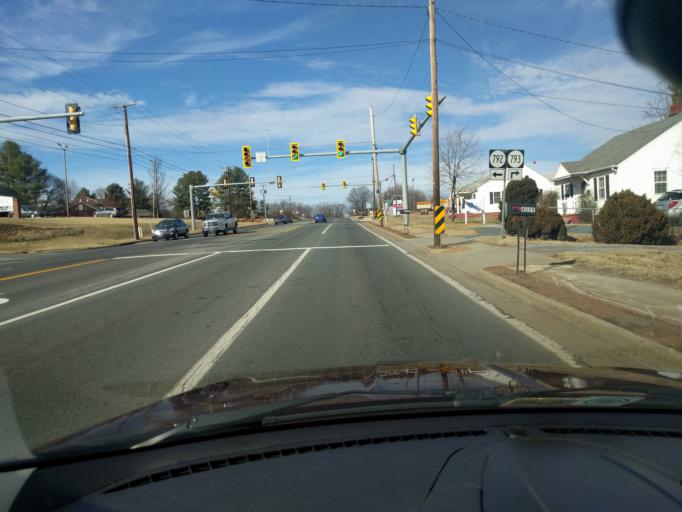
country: US
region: Virginia
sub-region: Amherst County
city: Madison Heights
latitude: 37.4692
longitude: -79.1195
